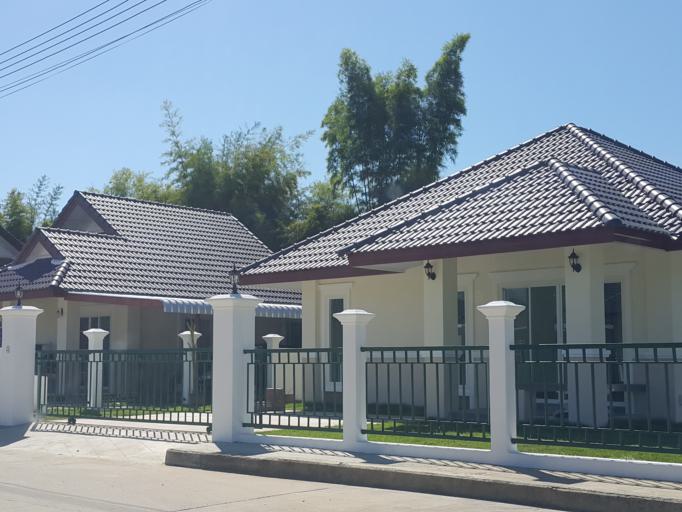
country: TH
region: Chiang Mai
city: San Sai
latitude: 18.7947
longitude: 99.0617
